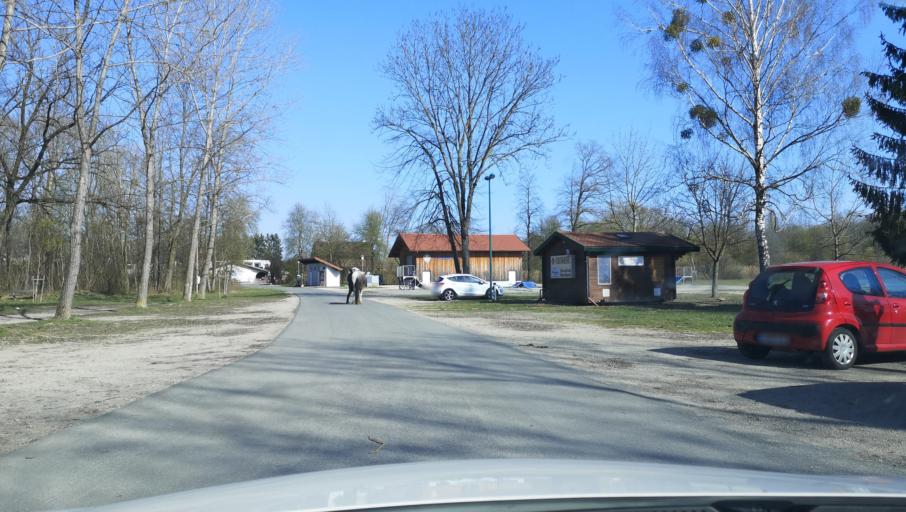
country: AT
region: Lower Austria
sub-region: Politischer Bezirk Melk
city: Blindenmarkt
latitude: 48.1183
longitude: 14.9895
